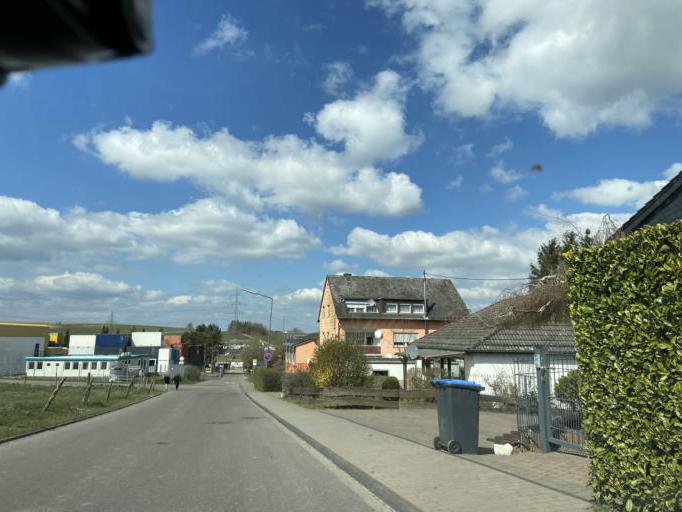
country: DE
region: Rheinland-Pfalz
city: Aach
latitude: 49.7781
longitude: 6.5811
